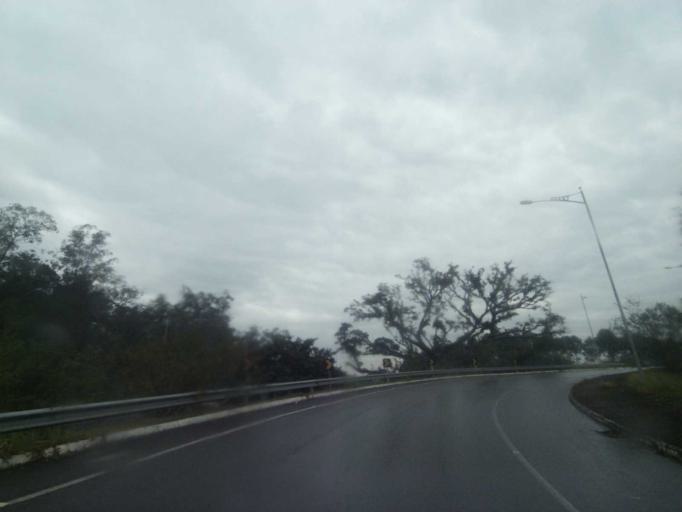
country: BR
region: Rio Grande do Sul
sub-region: Sao Leopoldo
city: Sao Leopoldo
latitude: -29.7879
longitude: -51.1622
